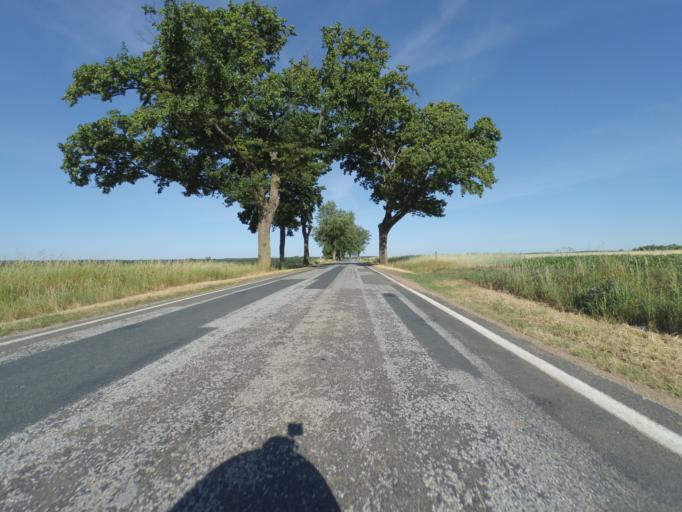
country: DE
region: Brandenburg
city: Gerdshagen
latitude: 53.3715
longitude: 12.1680
